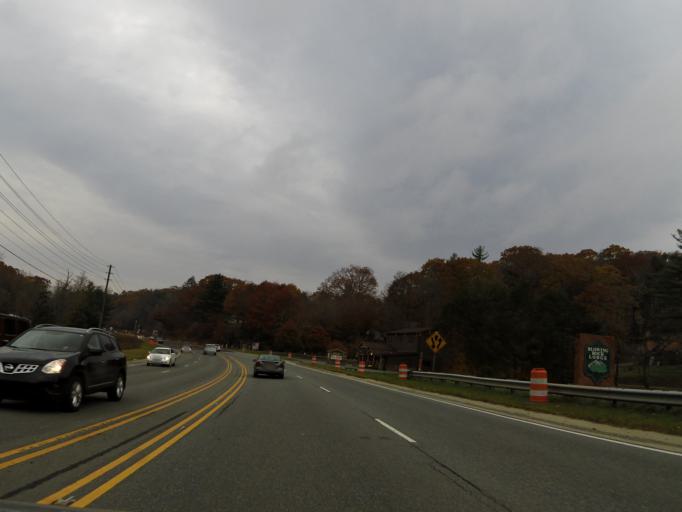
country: US
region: North Carolina
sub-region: Watauga County
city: Blowing Rock
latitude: 36.1515
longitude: -81.6564
